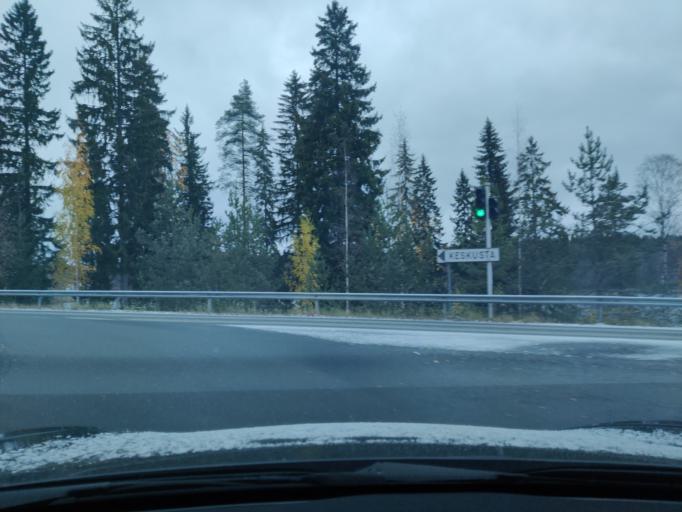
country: FI
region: Northern Savo
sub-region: Kuopio
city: Kuopio
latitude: 62.8423
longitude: 27.6340
